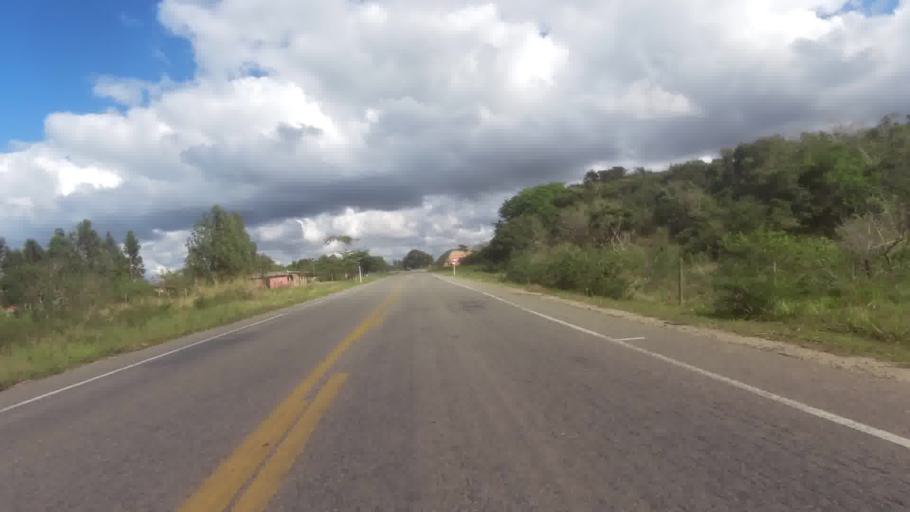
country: BR
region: Espirito Santo
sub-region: Marataizes
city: Marataizes
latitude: -21.1851
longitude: -40.9287
